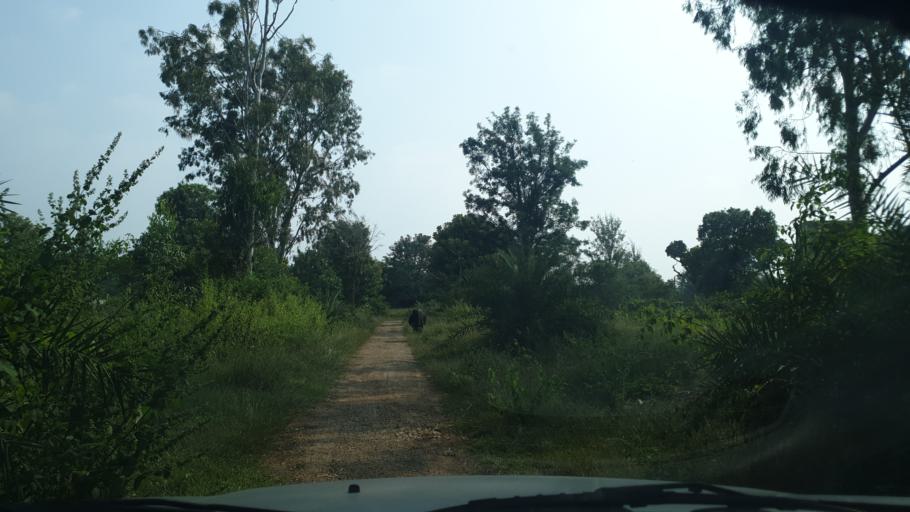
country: IN
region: Karnataka
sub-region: Bangalore Urban
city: Yelahanka
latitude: 13.0736
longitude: 77.6668
